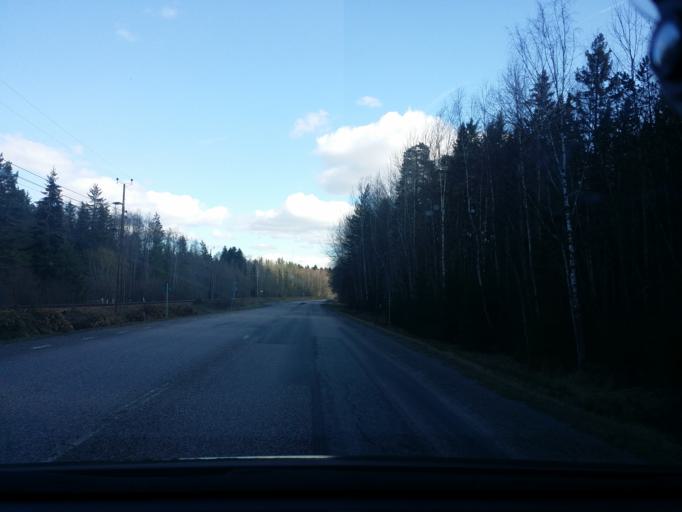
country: SE
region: Vaestmanland
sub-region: Sala Kommun
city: Sala
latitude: 59.9480
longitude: 16.5396
